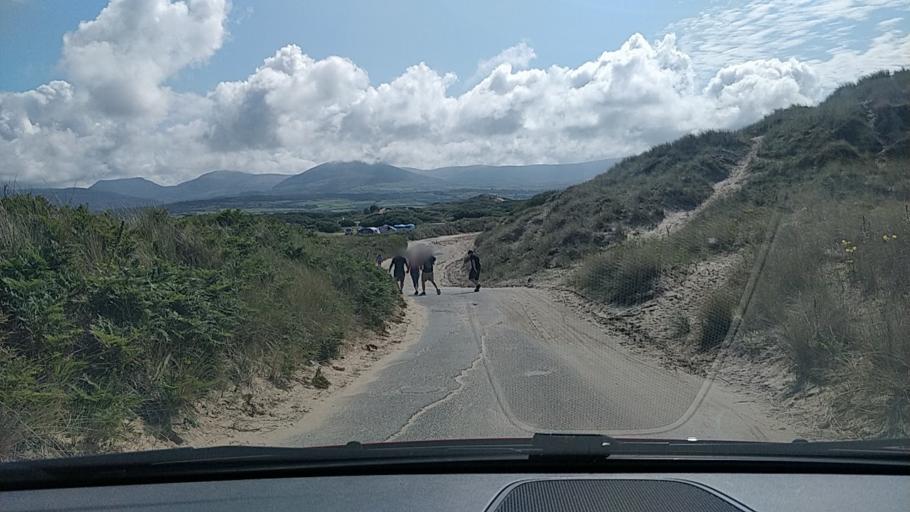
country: GB
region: Wales
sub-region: Gwynedd
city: Llanfair
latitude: 52.8128
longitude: -4.1504
